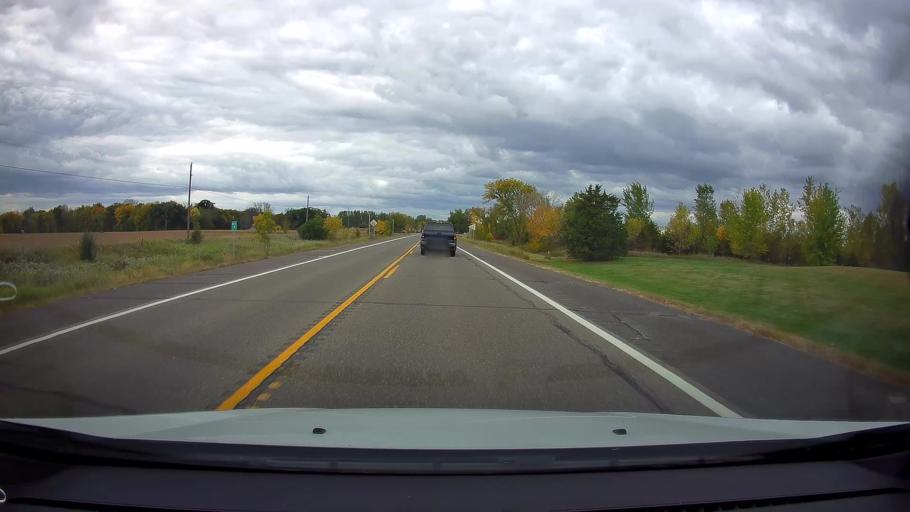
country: US
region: Minnesota
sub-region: Chisago County
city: Chisago City
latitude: 45.3515
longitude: -92.9117
